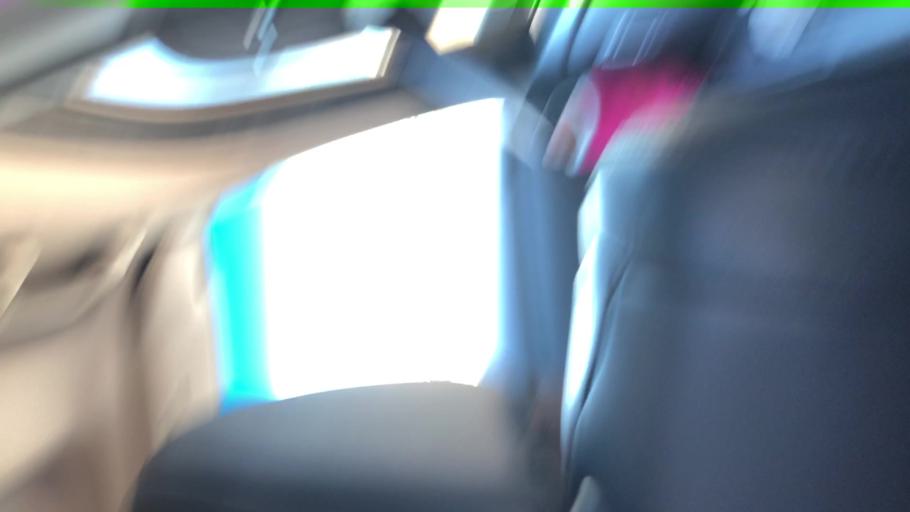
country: US
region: Texas
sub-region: Randall County
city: Canyon
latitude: 34.9984
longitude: -101.8958
